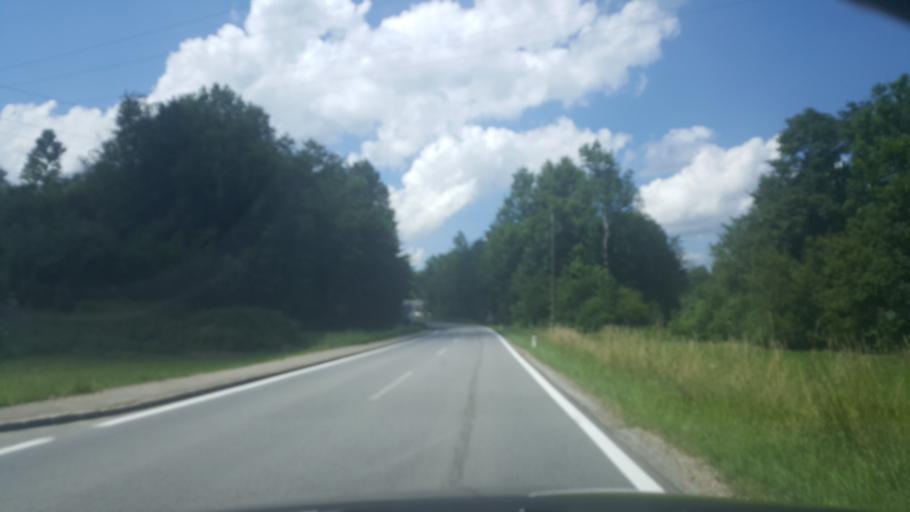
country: AT
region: Upper Austria
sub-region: Politischer Bezirk Vocklabruck
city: Gampern
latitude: 47.9929
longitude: 13.5487
